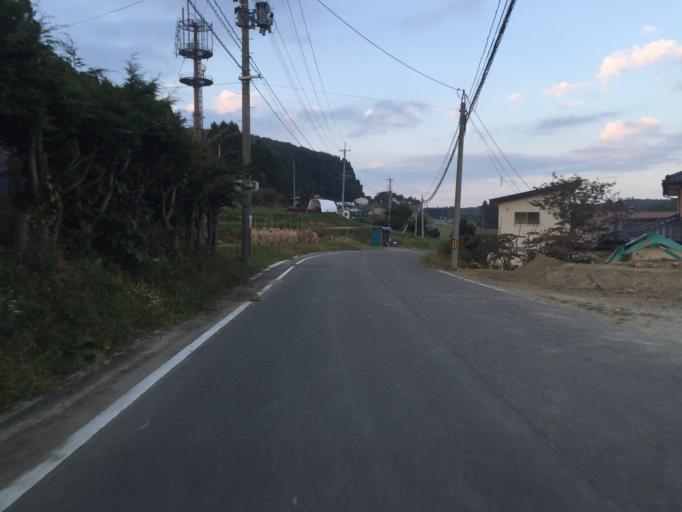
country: JP
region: Fukushima
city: Nihommatsu
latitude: 37.6104
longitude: 140.3566
